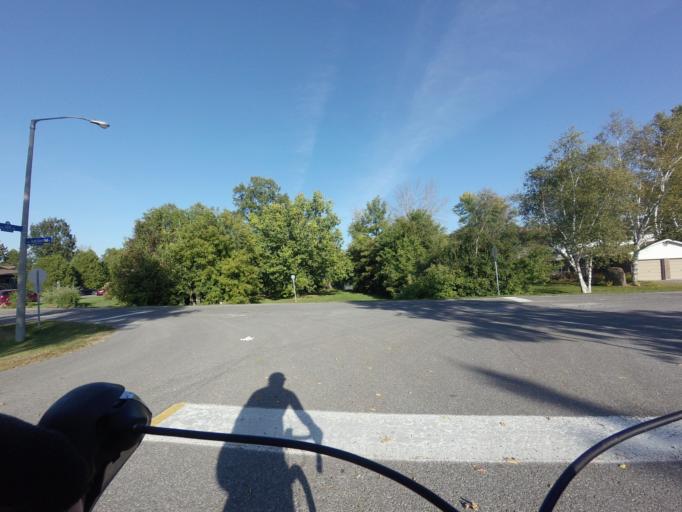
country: CA
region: Ontario
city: Bells Corners
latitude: 45.2265
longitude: -75.6726
